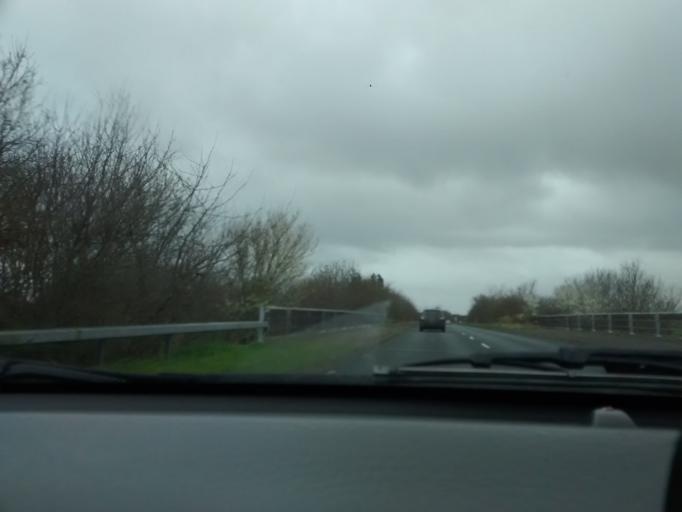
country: GB
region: England
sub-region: Suffolk
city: Felixstowe
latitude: 51.9748
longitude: 1.3412
